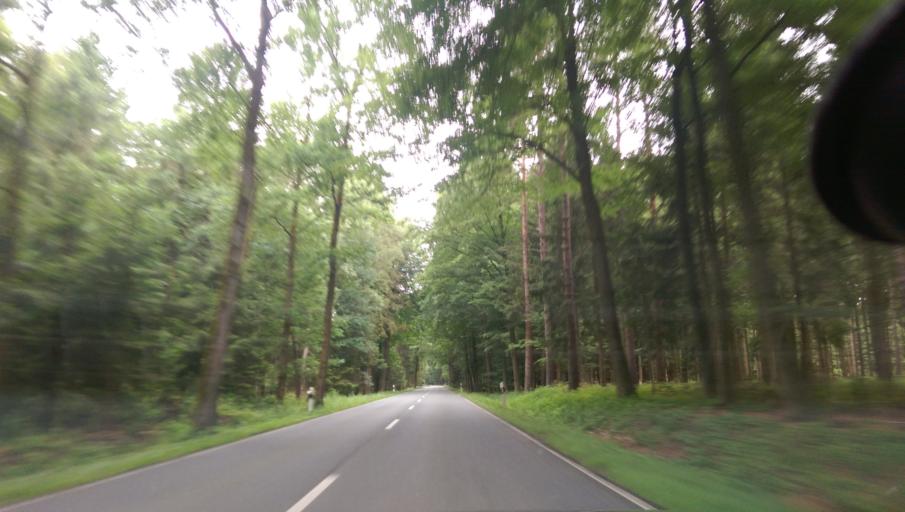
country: DE
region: Lower Saxony
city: Bomlitz
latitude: 52.9512
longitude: 9.6674
